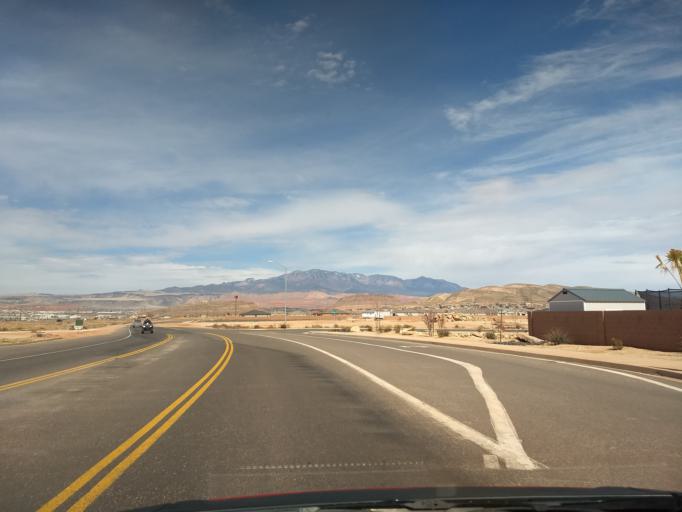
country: US
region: Utah
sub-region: Washington County
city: Washington
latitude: 37.0734
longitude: -113.4942
